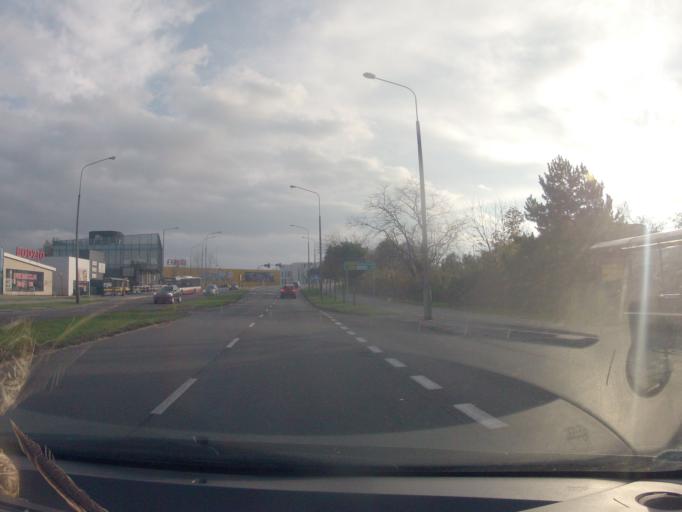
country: PL
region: Opole Voivodeship
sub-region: Powiat opolski
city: Opole
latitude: 50.6700
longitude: 17.9506
